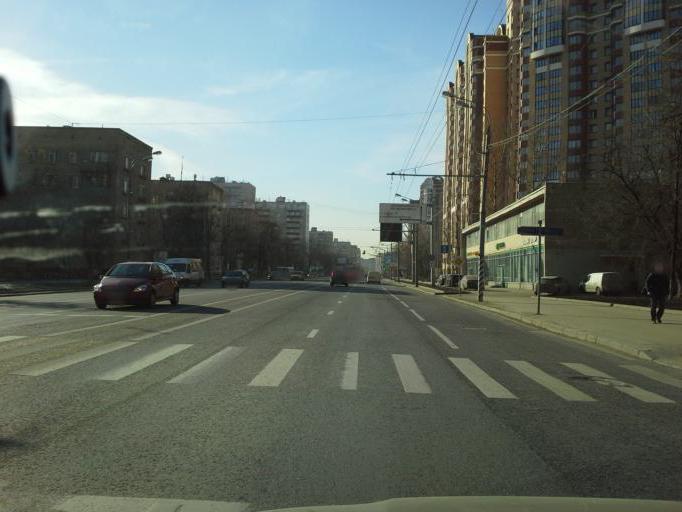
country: RU
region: Moscow
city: Taganskiy
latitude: 55.7375
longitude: 37.6879
